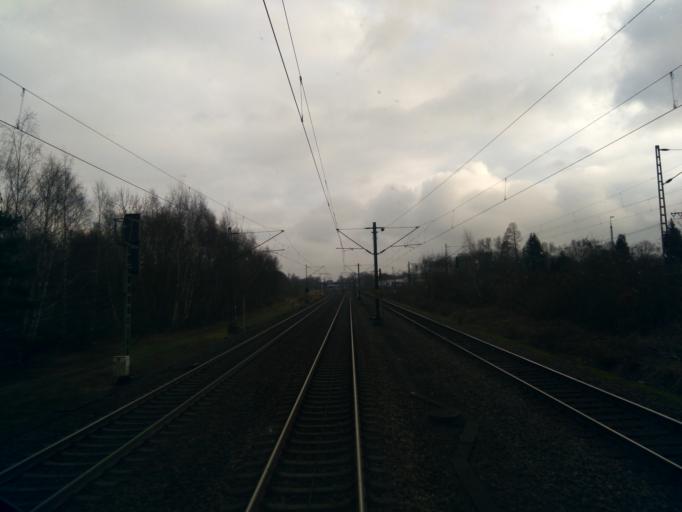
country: DE
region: Hamburg
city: Harburg
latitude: 53.4287
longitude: 10.0242
